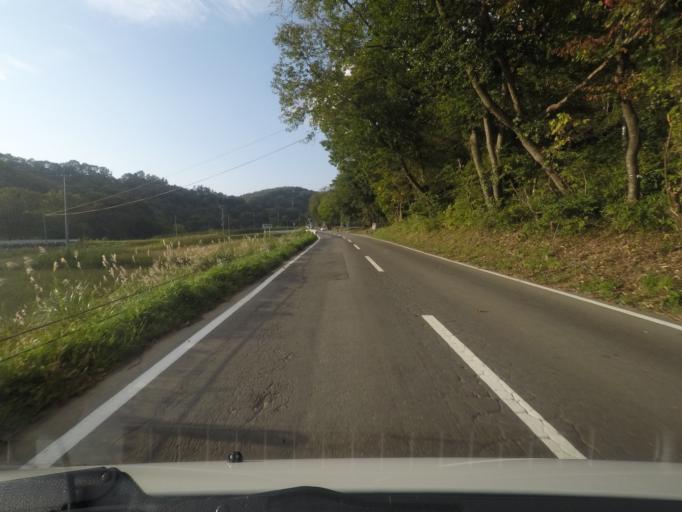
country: JP
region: Fukushima
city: Funehikimachi-funehiki
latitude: 37.5903
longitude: 140.6895
